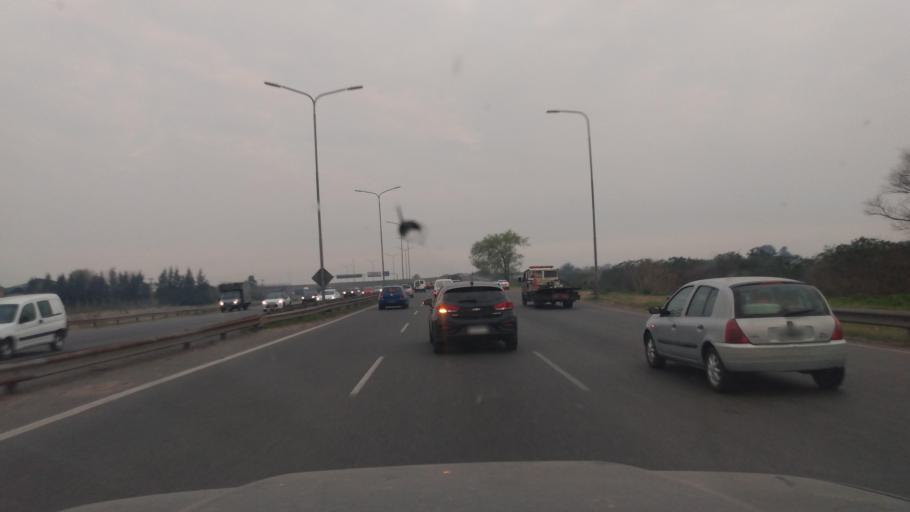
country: AR
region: Buenos Aires
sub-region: Partido de Tigre
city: Tigre
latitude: -34.4923
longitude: -58.5958
